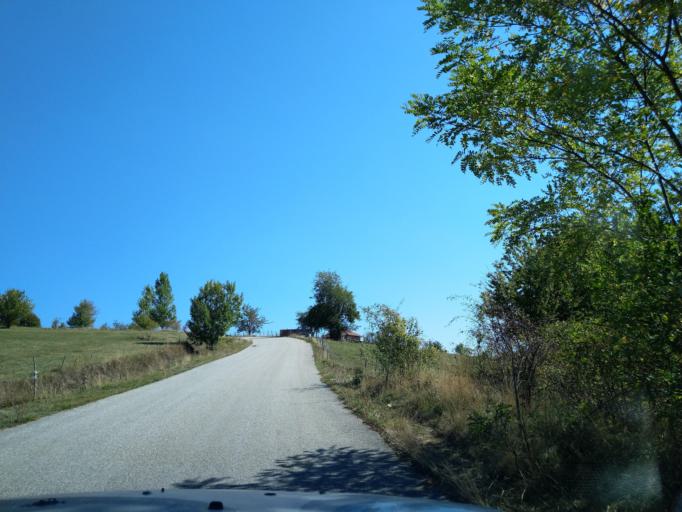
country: RS
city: Sokolovica
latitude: 43.2513
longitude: 20.3189
